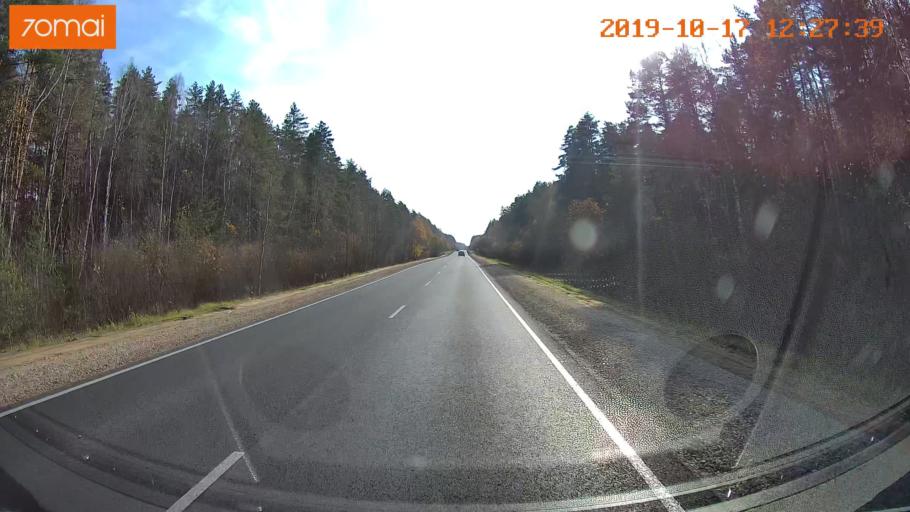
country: RU
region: Rjazan
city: Syntul
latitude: 55.0006
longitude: 41.2643
